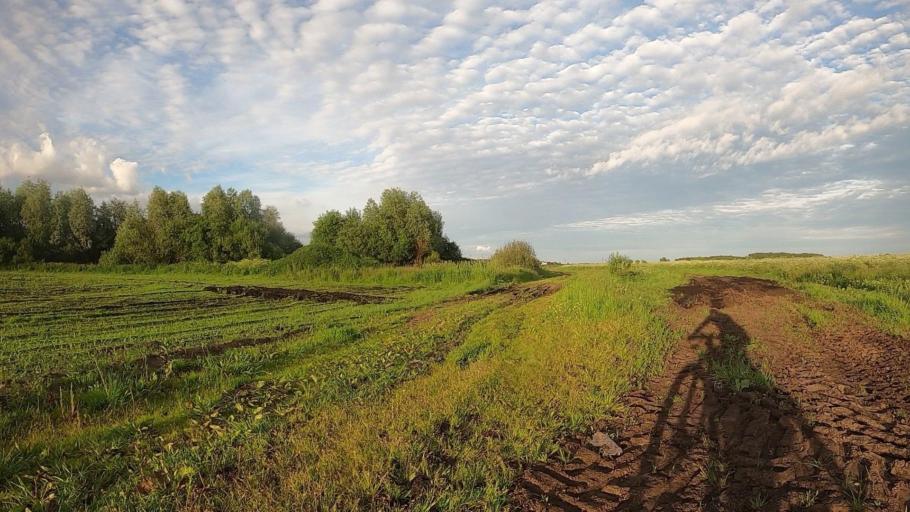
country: LV
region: Olaine
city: Olaine
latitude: 56.8665
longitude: 23.9653
